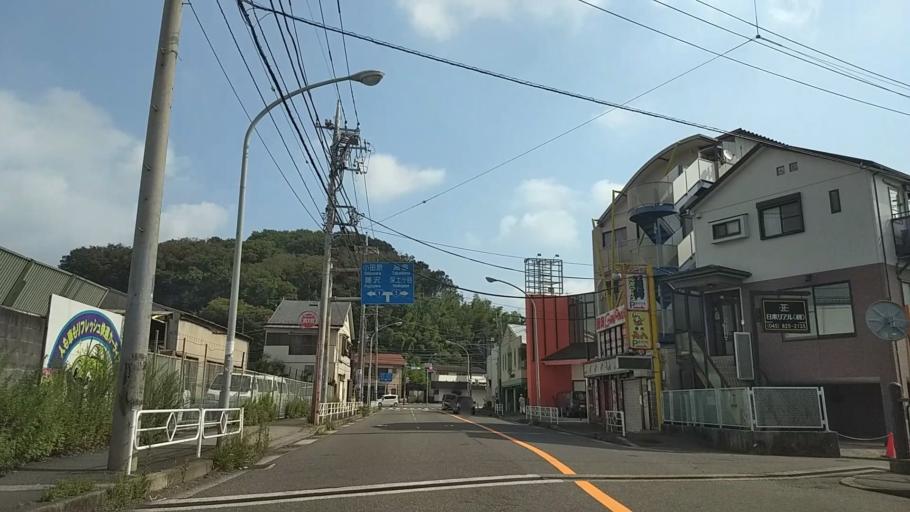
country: JP
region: Kanagawa
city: Yokohama
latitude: 35.4195
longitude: 139.5617
